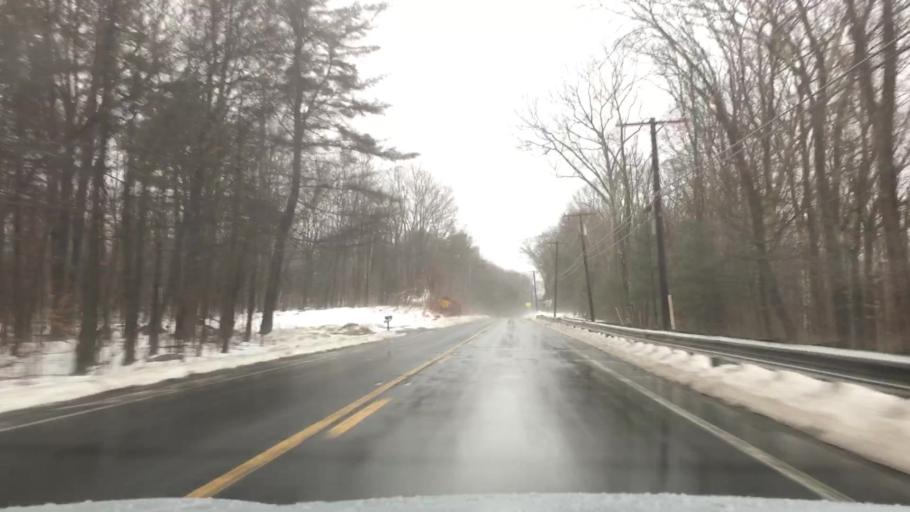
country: US
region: Massachusetts
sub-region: Hampshire County
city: Belchertown
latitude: 42.3235
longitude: -72.4053
